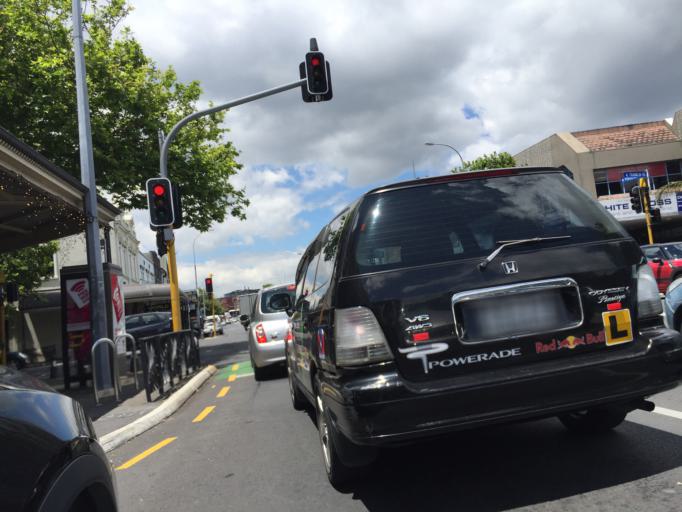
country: NZ
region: Auckland
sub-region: Auckland
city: Auckland
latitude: -36.8531
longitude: 174.7454
